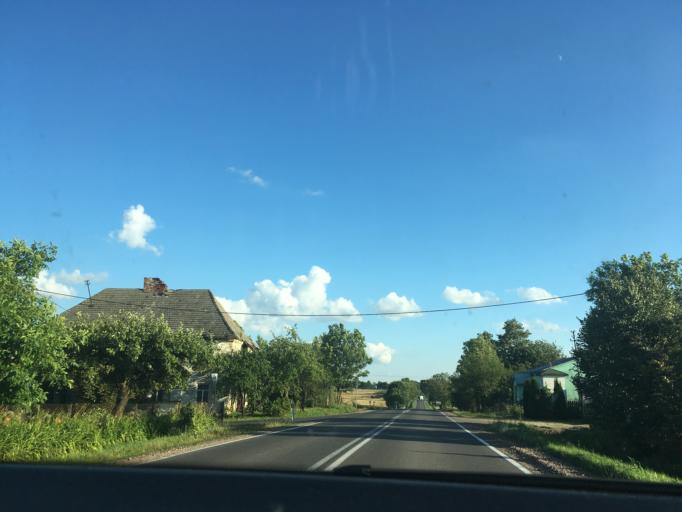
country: PL
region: Masovian Voivodeship
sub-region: Powiat losicki
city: Sarnaki
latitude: 52.2699
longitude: 22.8356
